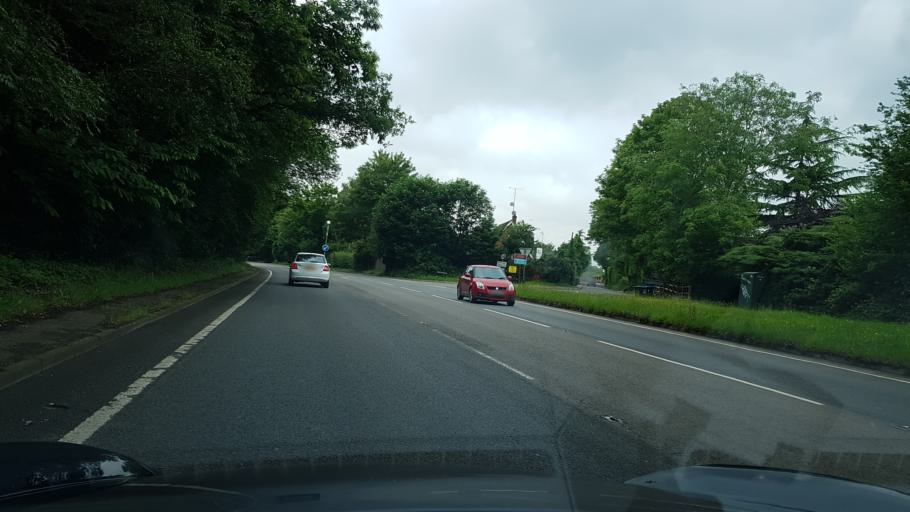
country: GB
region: England
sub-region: West Sussex
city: Copthorne
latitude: 51.1372
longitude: -0.1041
